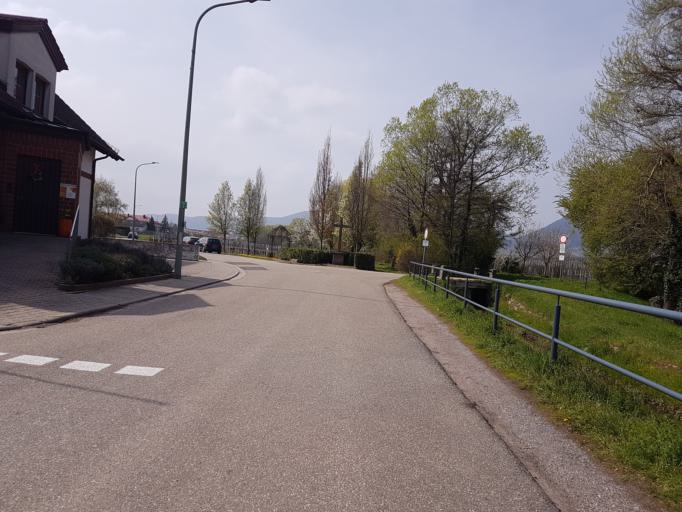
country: DE
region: Rheinland-Pfalz
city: Roschbach
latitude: 49.2588
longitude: 8.1195
